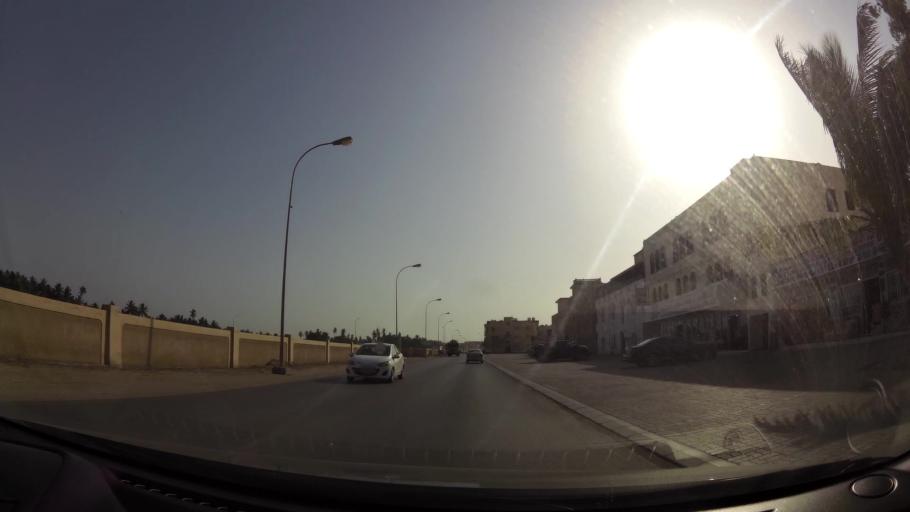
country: OM
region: Zufar
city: Salalah
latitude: 17.0063
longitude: 54.0768
